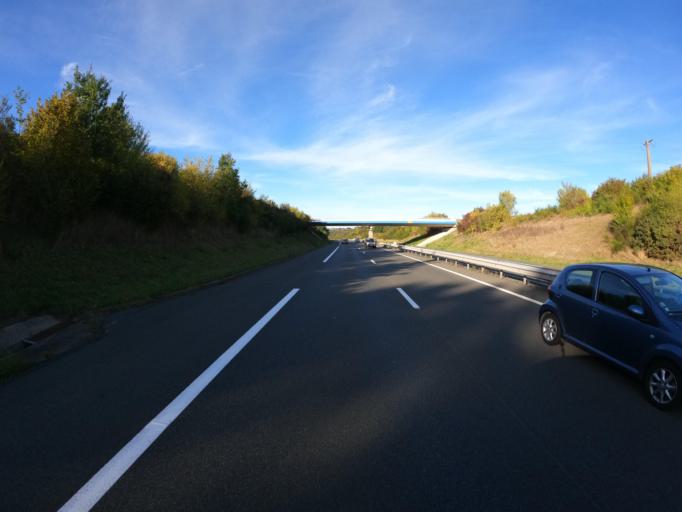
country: FR
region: Pays de la Loire
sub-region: Departement de Maine-et-Loire
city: Saint-Lambert-du-Lattay
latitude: 47.2979
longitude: -0.6100
